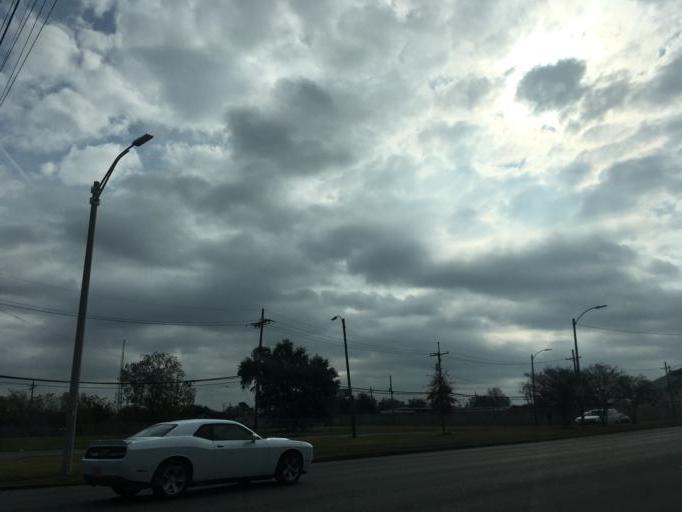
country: US
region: Louisiana
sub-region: Orleans Parish
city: New Orleans
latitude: 29.9888
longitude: -90.0587
